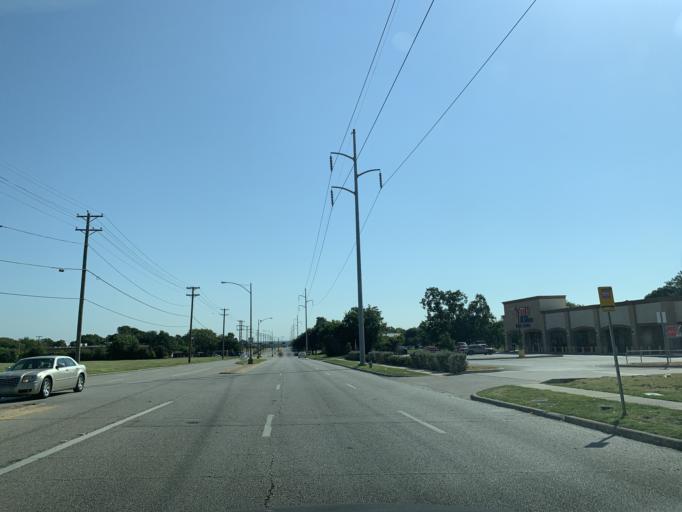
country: US
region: Texas
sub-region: Dallas County
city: Hutchins
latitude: 32.6730
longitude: -96.7623
